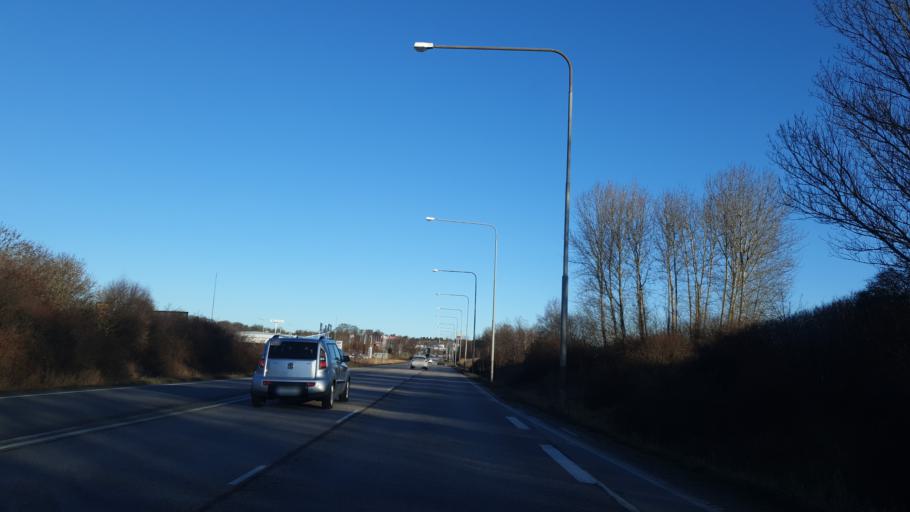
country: SE
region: Blekinge
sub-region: Karlskrona Kommun
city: Karlskrona
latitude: 56.1979
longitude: 15.6340
